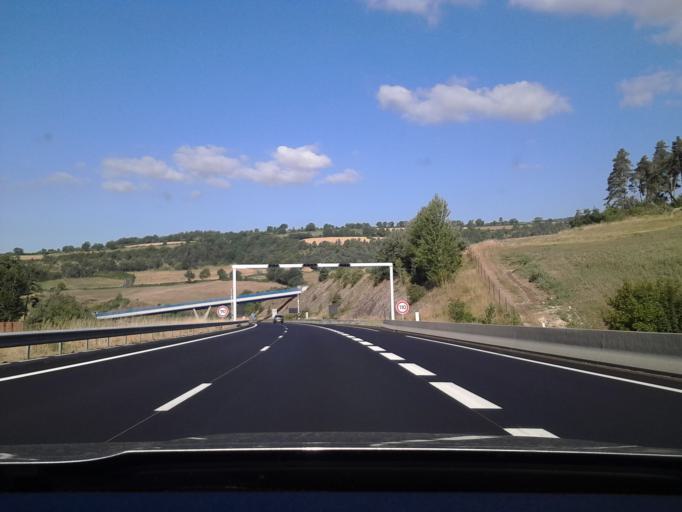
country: FR
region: Languedoc-Roussillon
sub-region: Departement de la Lozere
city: La Canourgue
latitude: 44.4884
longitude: 3.2101
